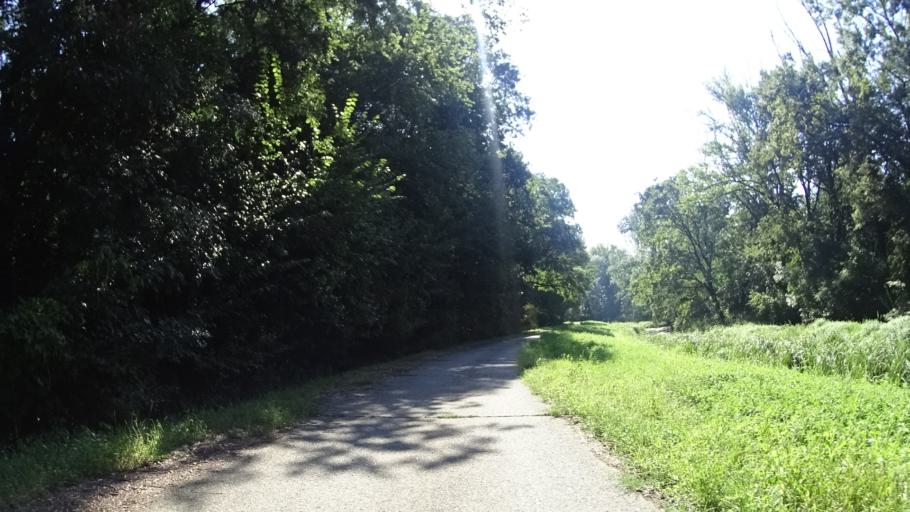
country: SK
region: Trnavsky
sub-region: Okres Skalica
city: Holic
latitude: 48.8198
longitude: 17.1346
